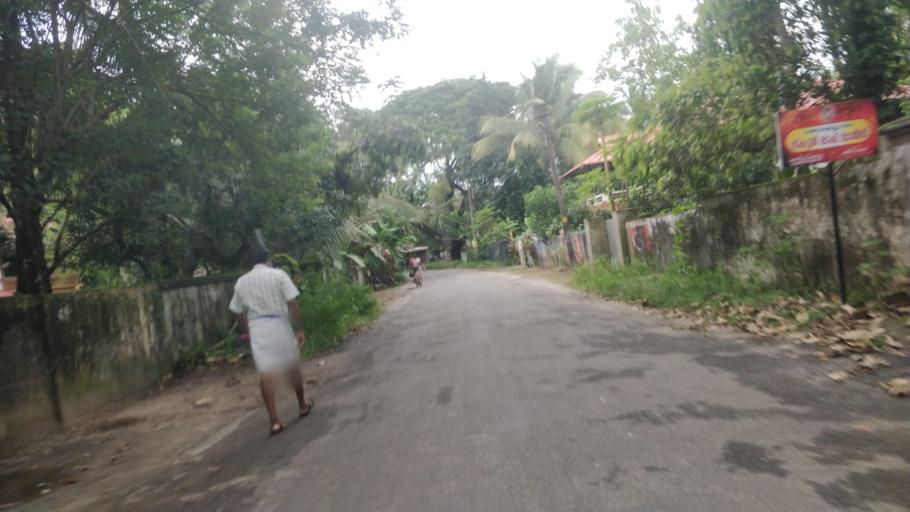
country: IN
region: Kerala
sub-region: Alappuzha
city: Shertallai
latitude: 9.6958
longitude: 76.3602
